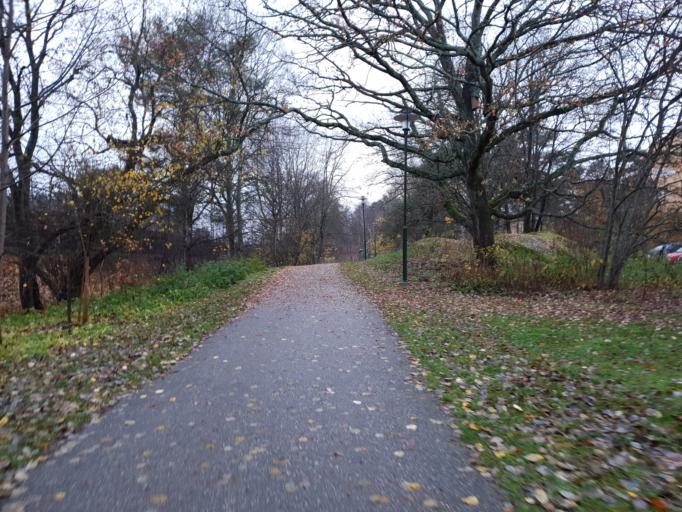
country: SE
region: Stockholm
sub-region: Stockholms Kommun
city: Arsta
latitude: 59.2416
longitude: 18.0840
